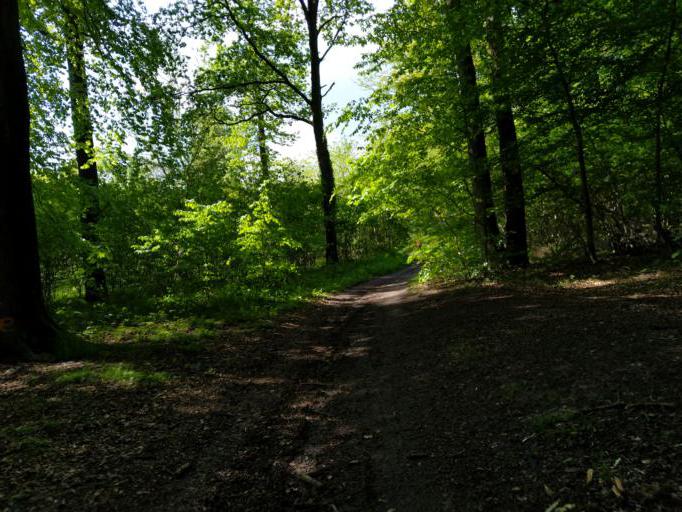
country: BE
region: Wallonia
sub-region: Province du Hainaut
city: Mons
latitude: 50.4829
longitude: 3.9333
